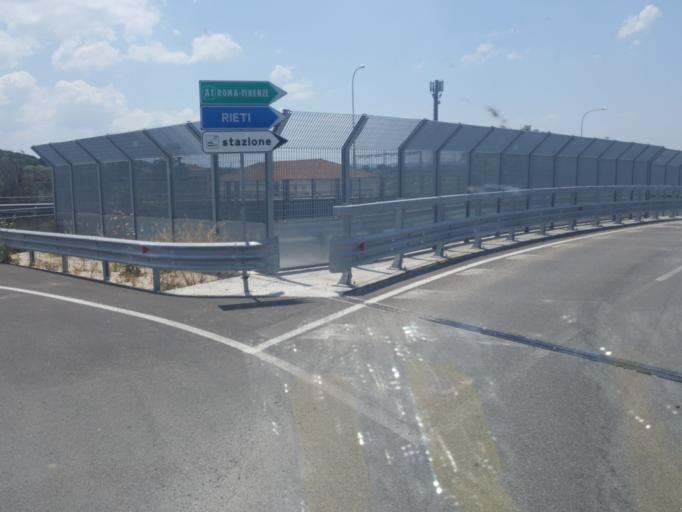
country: IT
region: Latium
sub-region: Citta metropolitana di Roma Capitale
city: Fiano Romano
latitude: 42.1624
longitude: 12.6472
